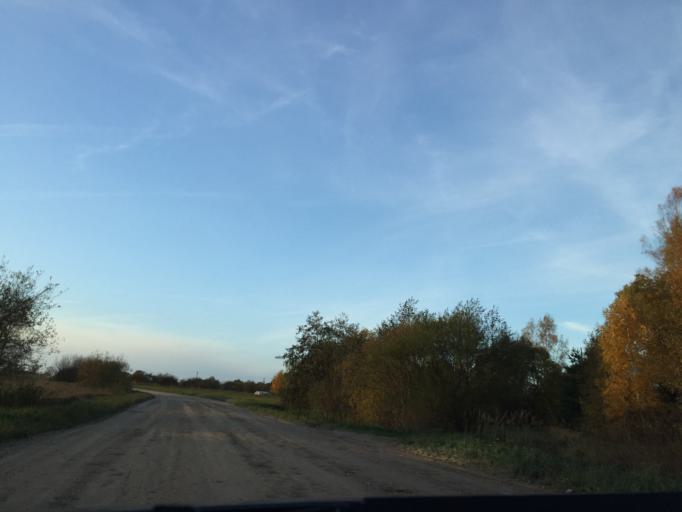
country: LV
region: Malpils
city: Malpils
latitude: 56.8902
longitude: 24.9480
